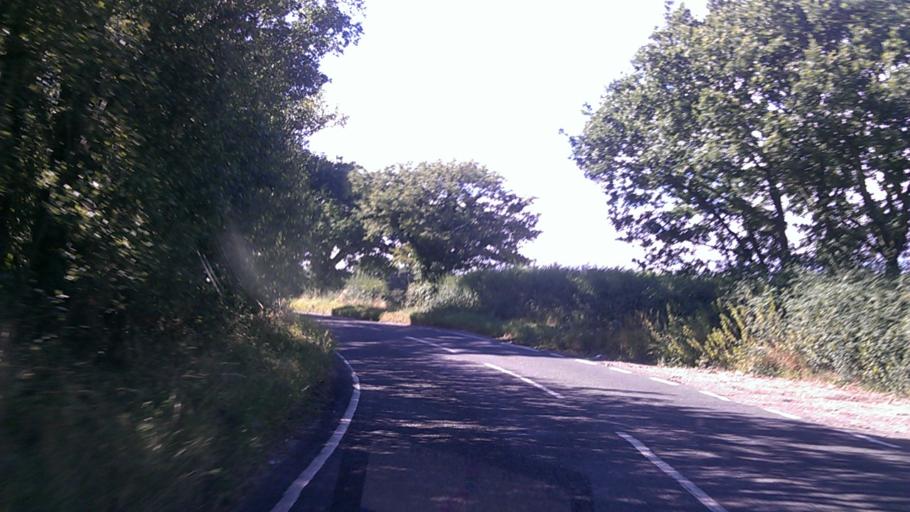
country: GB
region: England
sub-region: Essex
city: Layer de la Haye
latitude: 51.8447
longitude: 0.8851
